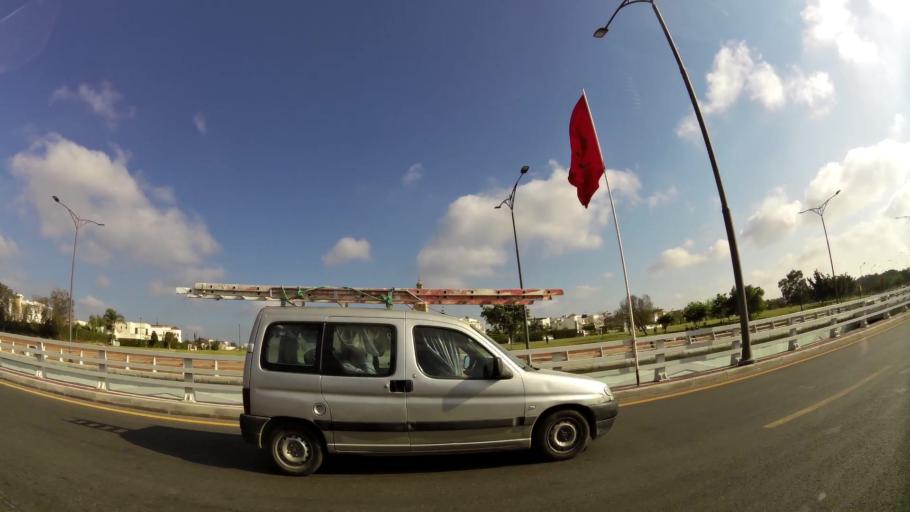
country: MA
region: Rabat-Sale-Zemmour-Zaer
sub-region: Skhirate-Temara
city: Temara
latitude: 33.9475
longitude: -6.8704
